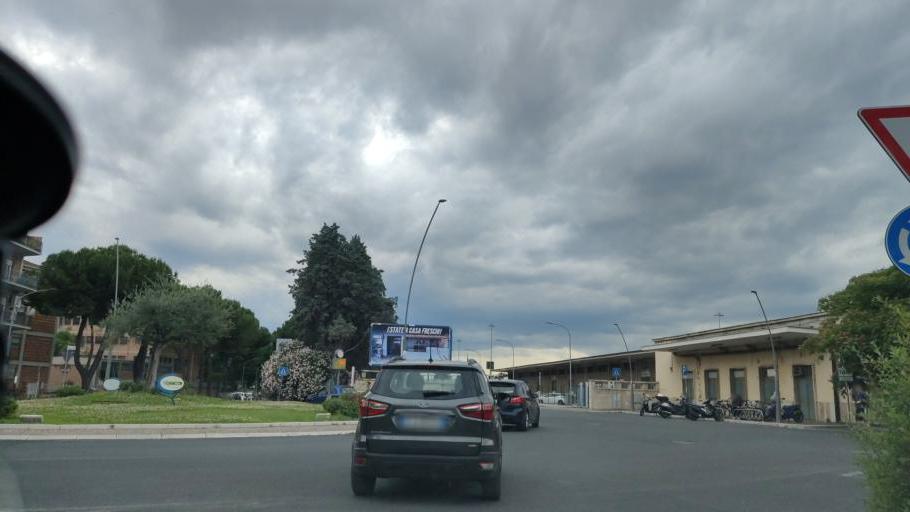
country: IT
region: Umbria
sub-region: Provincia di Terni
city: Terni
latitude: 42.5700
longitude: 12.6508
